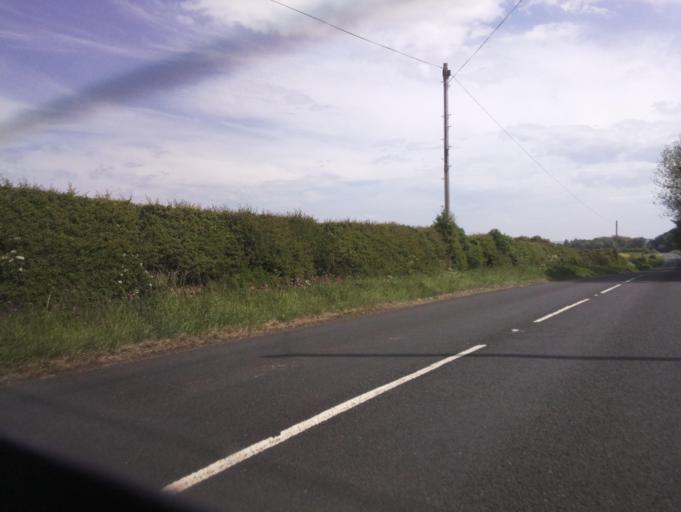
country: GB
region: England
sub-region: Northumberland
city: Alnwick
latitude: 55.4353
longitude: -1.7085
